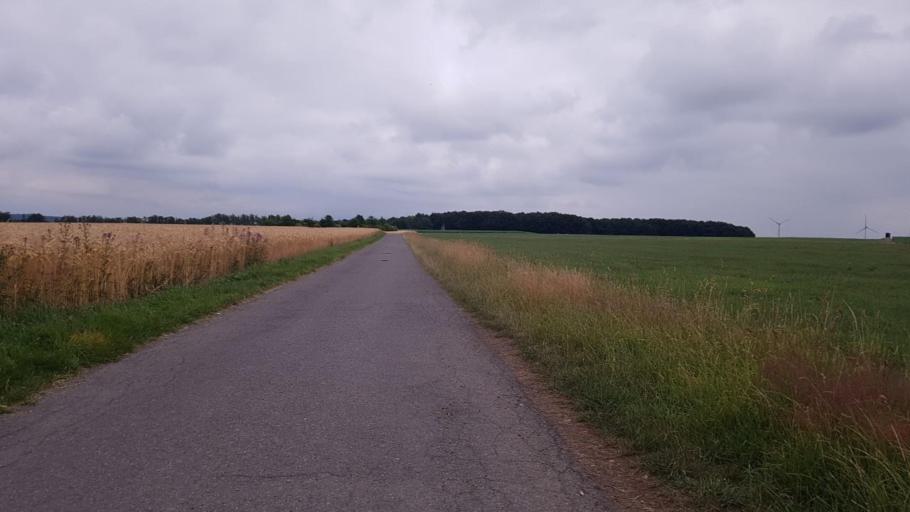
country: DE
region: North Rhine-Westphalia
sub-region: Regierungsbezirk Koln
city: Hurtgenwald
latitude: 50.7337
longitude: 6.4011
